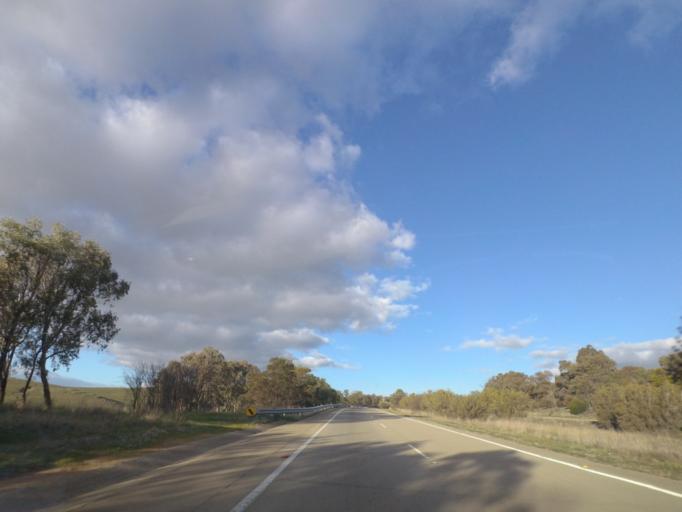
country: AU
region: New South Wales
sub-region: Yass Valley
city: Yass
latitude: -34.8029
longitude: 148.5538
